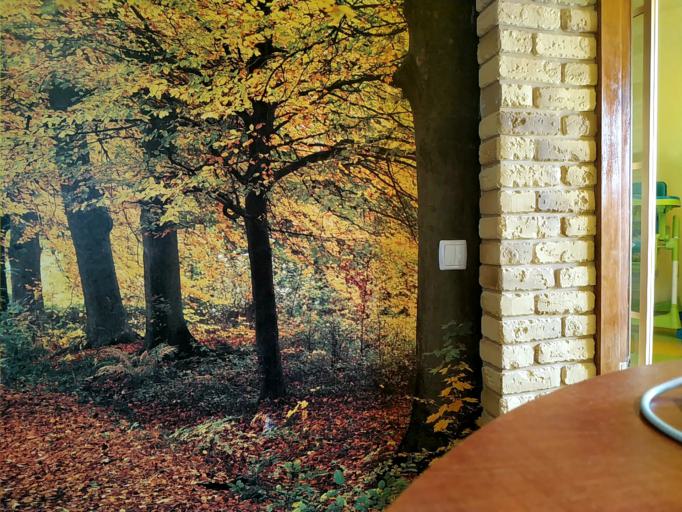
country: RU
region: Tverskaya
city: Kalashnikovo
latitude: 57.3342
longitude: 35.3320
